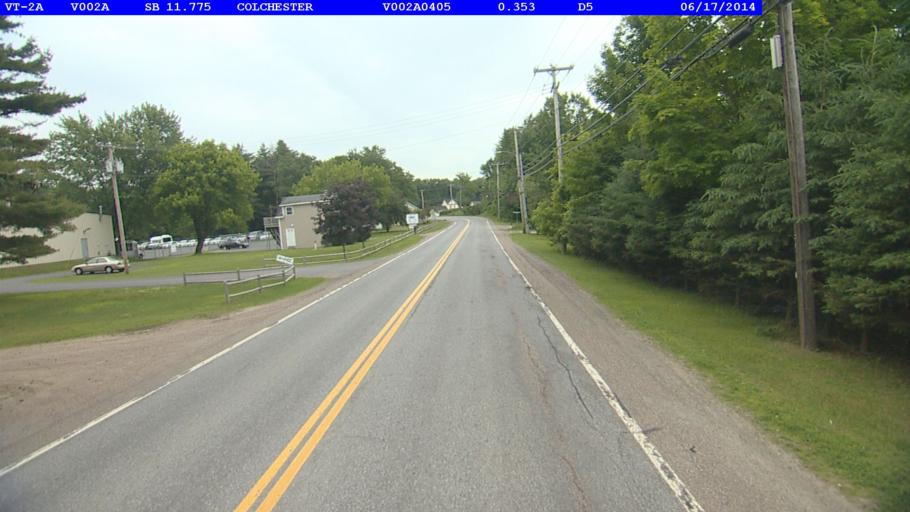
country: US
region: Vermont
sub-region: Chittenden County
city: Colchester
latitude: 44.5325
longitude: -73.1331
